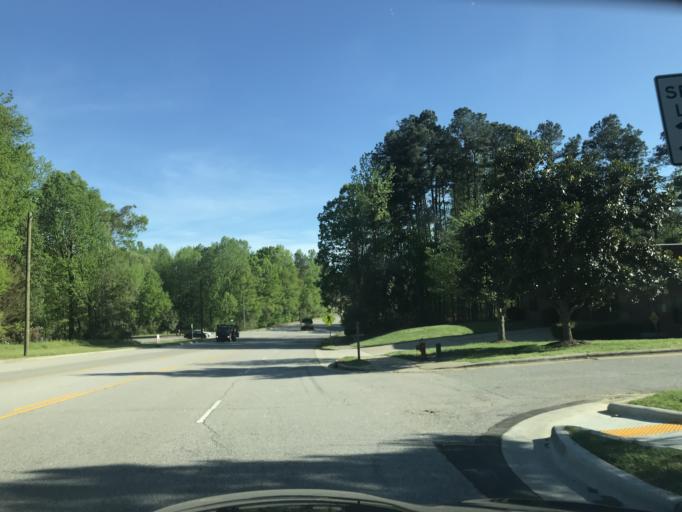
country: US
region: North Carolina
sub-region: Wake County
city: Knightdale
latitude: 35.8114
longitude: -78.5559
